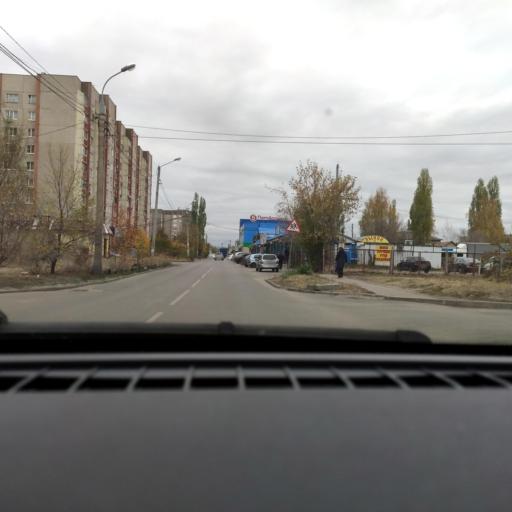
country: RU
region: Voronezj
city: Somovo
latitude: 51.7383
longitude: 39.2913
